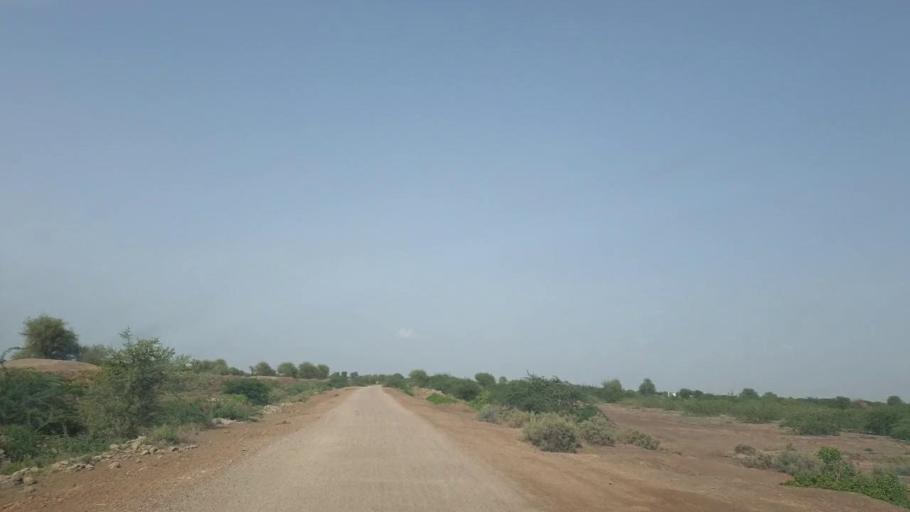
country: PK
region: Sindh
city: Tando Bago
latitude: 24.7989
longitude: 69.1627
